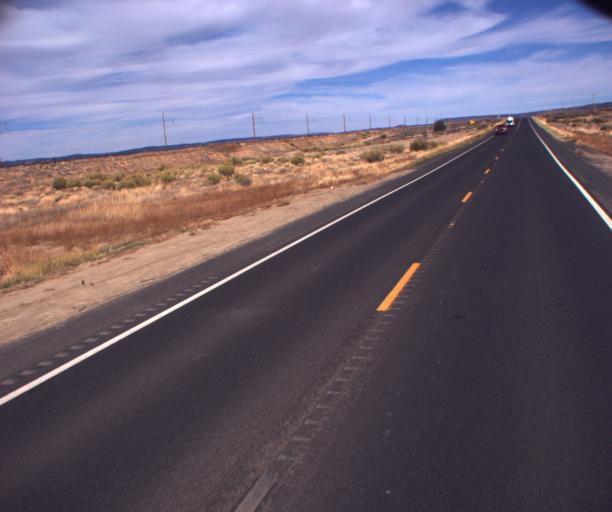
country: US
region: Arizona
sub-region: Navajo County
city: Kayenta
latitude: 36.5225
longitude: -110.5831
